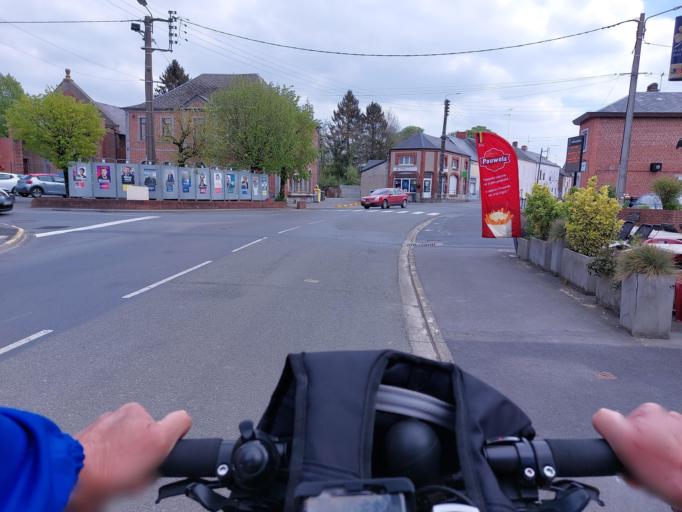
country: FR
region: Nord-Pas-de-Calais
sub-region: Departement du Nord
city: La Longueville
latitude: 50.2900
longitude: 3.8560
